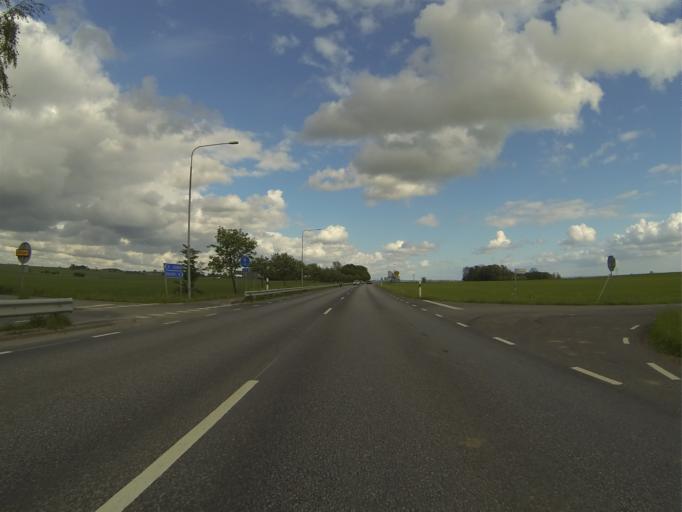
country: SE
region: Skane
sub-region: Staffanstorps Kommun
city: Staffanstorp
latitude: 55.6847
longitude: 13.2682
